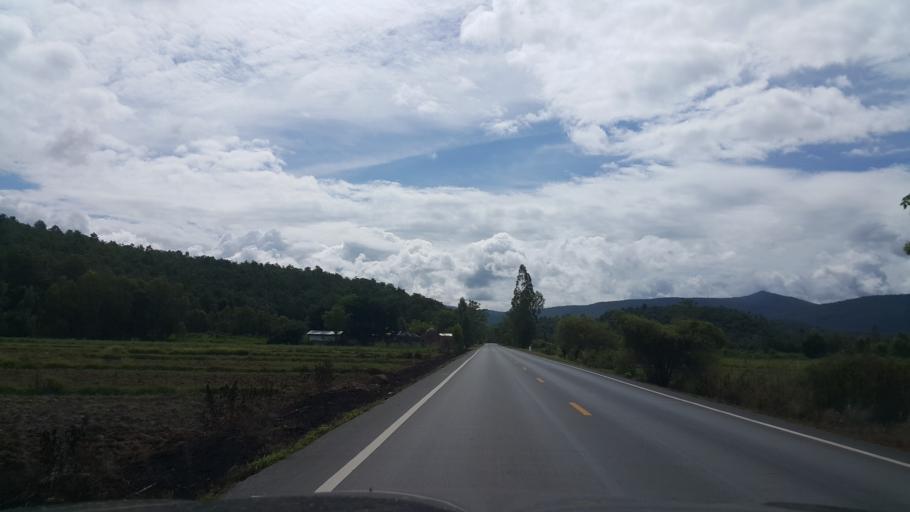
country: TH
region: Uttaradit
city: Thong Saen Khan
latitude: 17.3639
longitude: 100.2405
